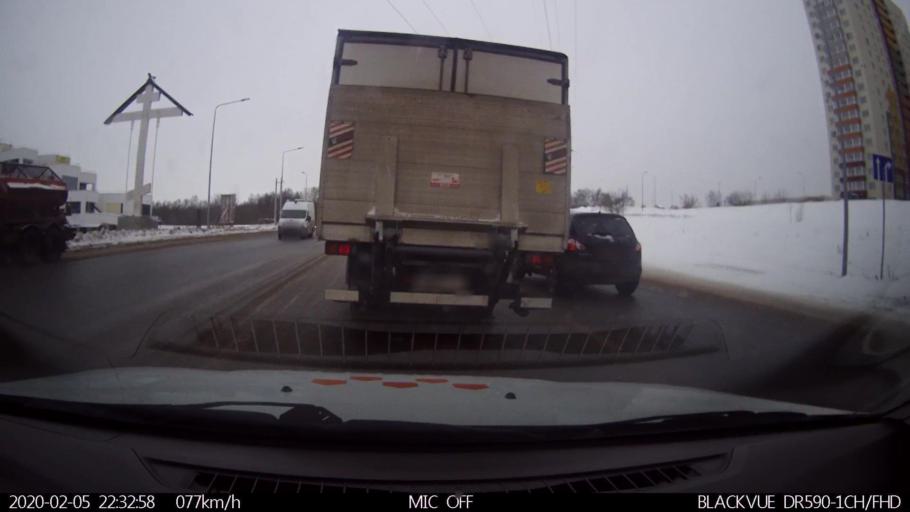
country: RU
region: Nizjnij Novgorod
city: Imeni Stepana Razina
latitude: 54.7371
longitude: 44.1991
